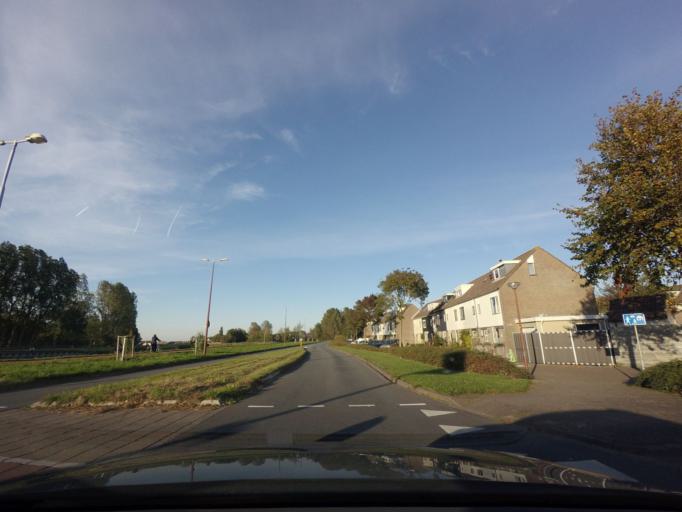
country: NL
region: North Holland
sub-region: Gemeente Alkmaar
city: Alkmaar
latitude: 52.6559
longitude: 4.7459
